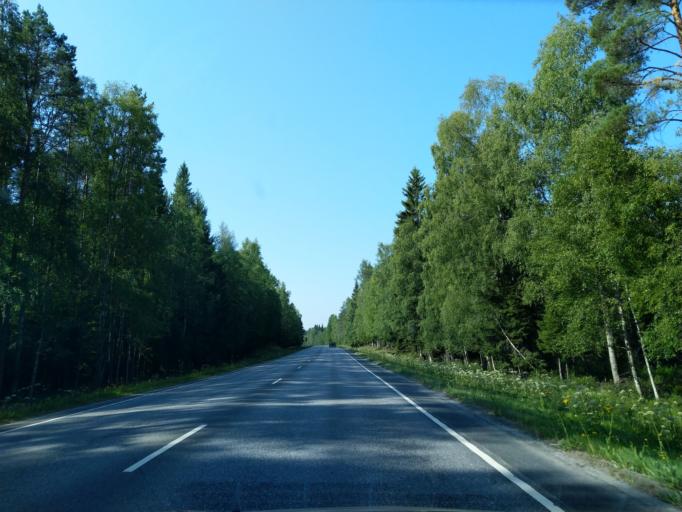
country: FI
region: Satakunta
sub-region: Pori
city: Noormarkku
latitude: 61.6142
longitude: 21.8935
